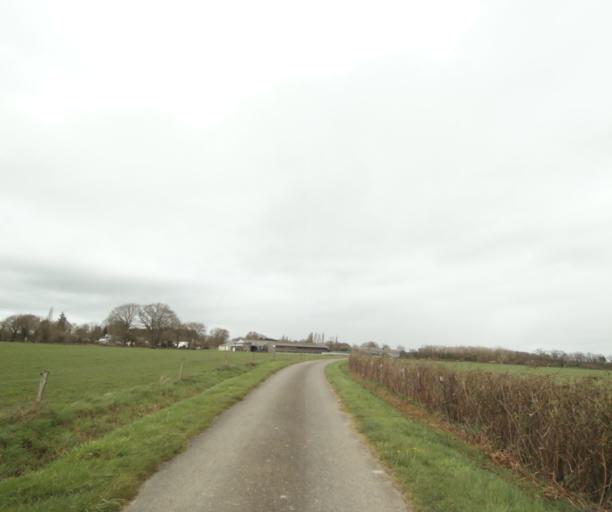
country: FR
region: Pays de la Loire
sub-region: Departement de la Loire-Atlantique
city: Bouvron
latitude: 47.4321
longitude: -1.8471
